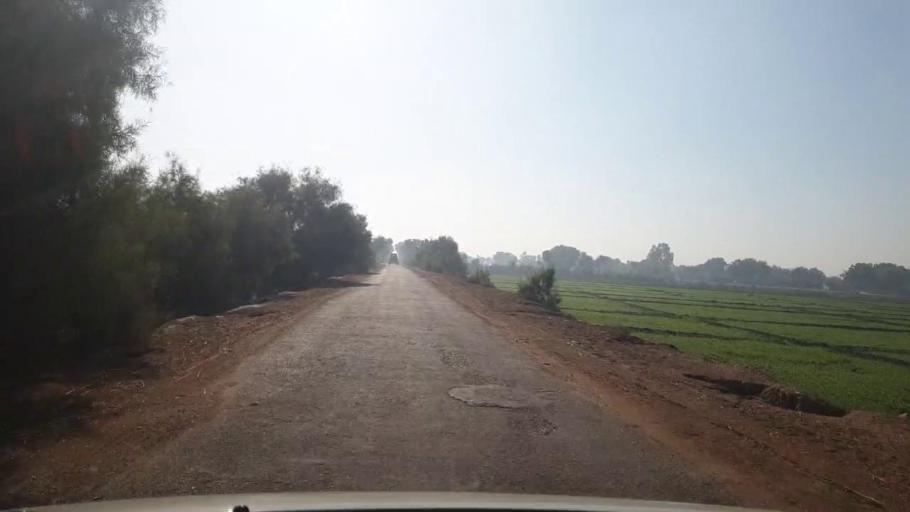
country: PK
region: Sindh
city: Dadu
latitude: 26.6598
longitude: 67.8202
